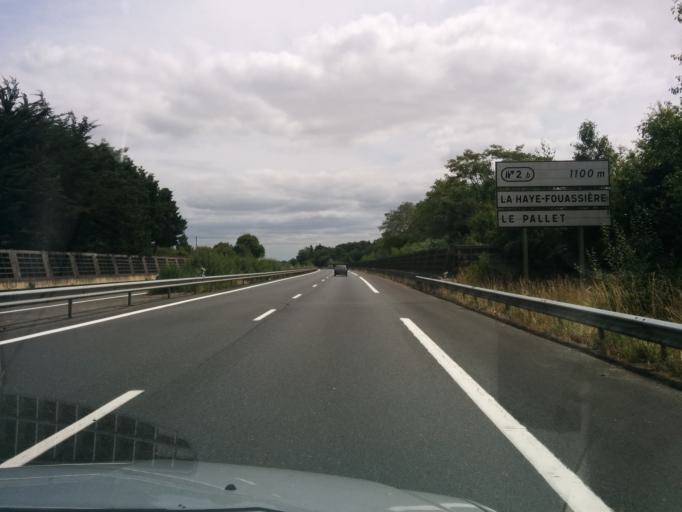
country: FR
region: Pays de la Loire
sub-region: Departement de la Loire-Atlantique
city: Haute-Goulaine
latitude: 47.1797
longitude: -1.4111
